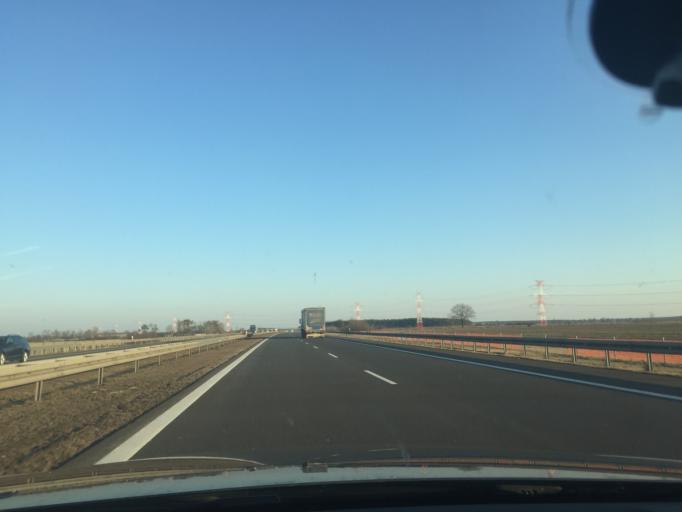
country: PL
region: Greater Poland Voivodeship
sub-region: Powiat wrzesinski
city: Kolaczkowo
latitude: 52.2874
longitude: 17.6761
